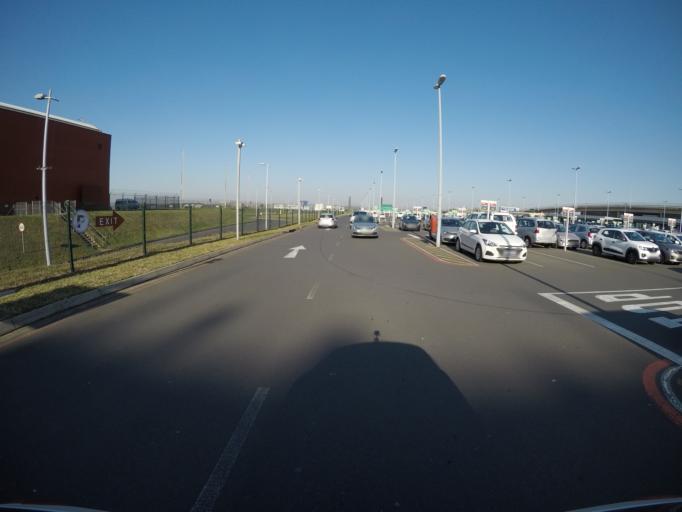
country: ZA
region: KwaZulu-Natal
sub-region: iLembe District Municipality
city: Ballitoville
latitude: -29.6203
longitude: 31.1040
